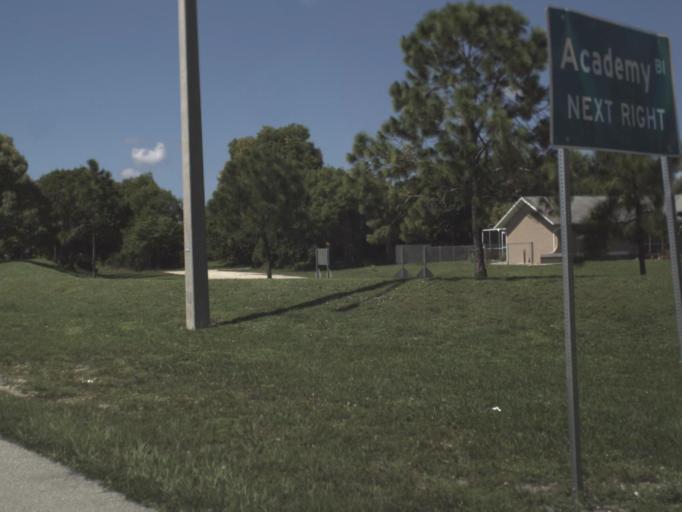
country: US
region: Florida
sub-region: Lee County
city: Cape Coral
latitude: 26.6055
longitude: -81.9571
